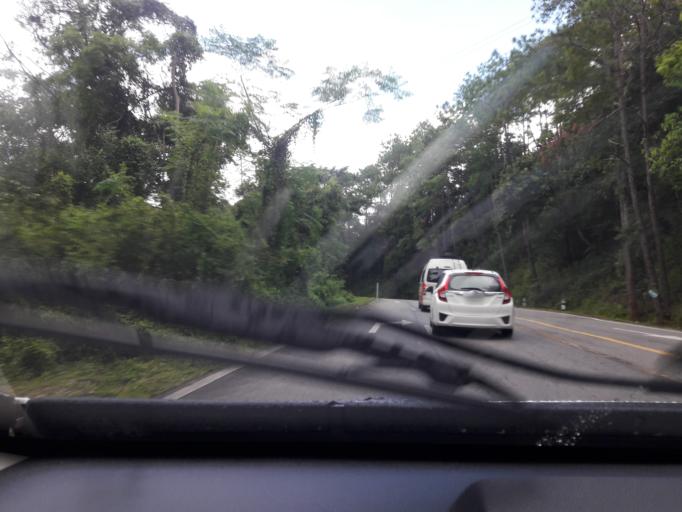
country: TH
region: Mae Hong Son
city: Mae Hi
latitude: 19.2316
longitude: 98.6677
